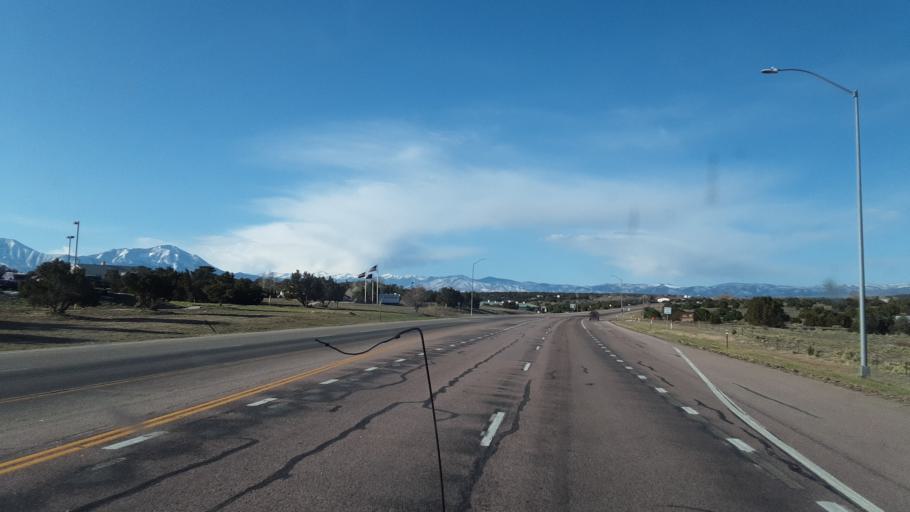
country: US
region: Colorado
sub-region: Huerfano County
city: Walsenburg
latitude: 37.6021
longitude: -104.8313
